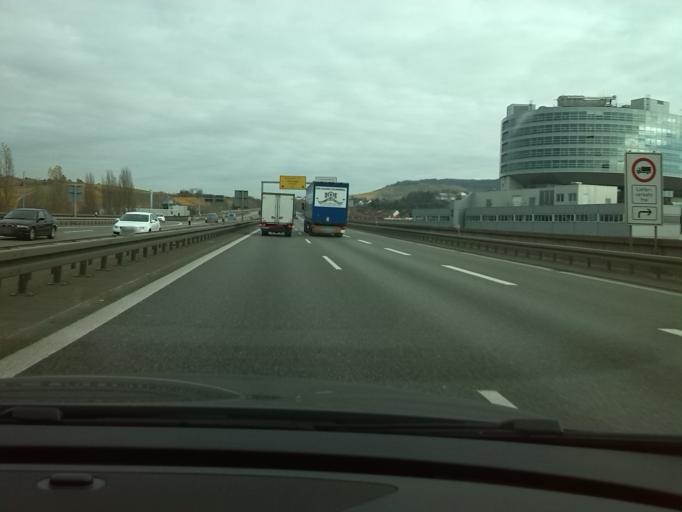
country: DE
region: Baden-Wuerttemberg
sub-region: Regierungsbezirk Stuttgart
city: Stuttgart-Ost
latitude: 48.7887
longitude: 9.2374
